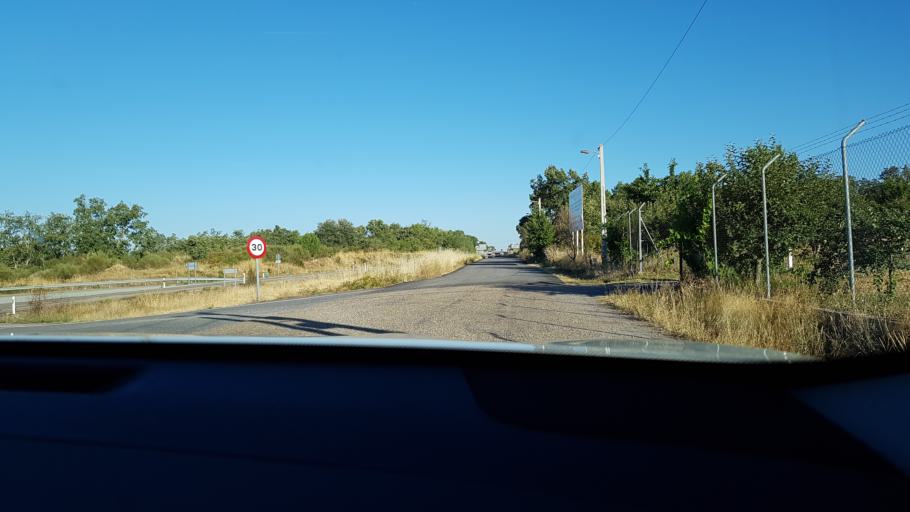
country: ES
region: Castille and Leon
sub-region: Provincia de Zamora
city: Samir de los Canos
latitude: 41.6586
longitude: -6.1957
